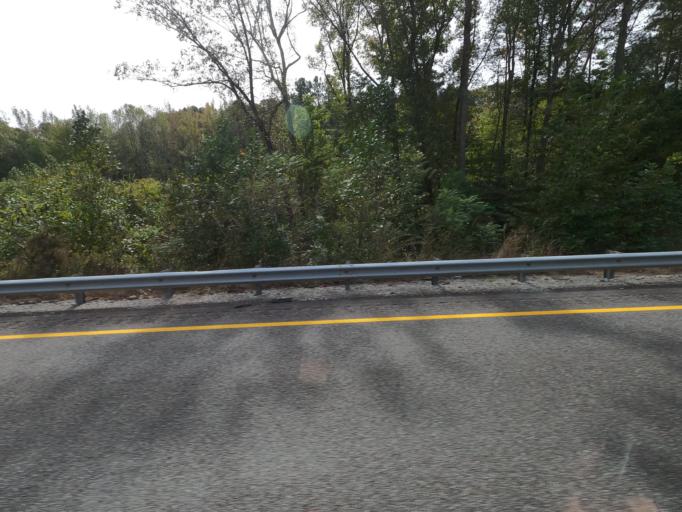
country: US
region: Tennessee
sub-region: Decatur County
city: Parsons
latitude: 35.8150
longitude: -88.2106
